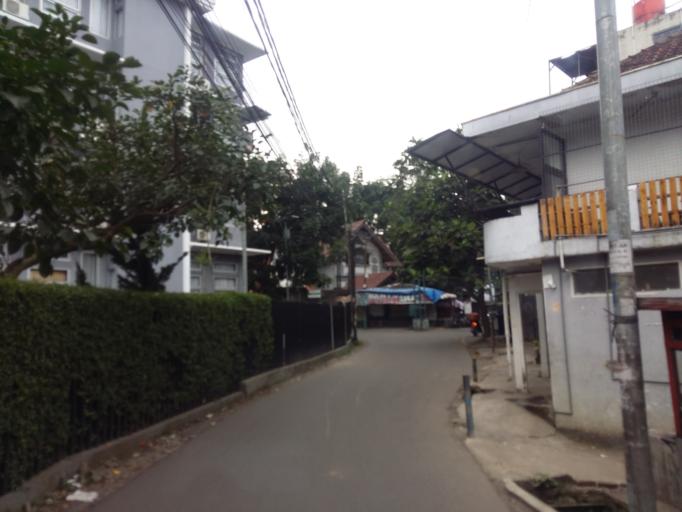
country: ID
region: West Java
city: Bandung
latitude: -6.8795
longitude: 107.6123
